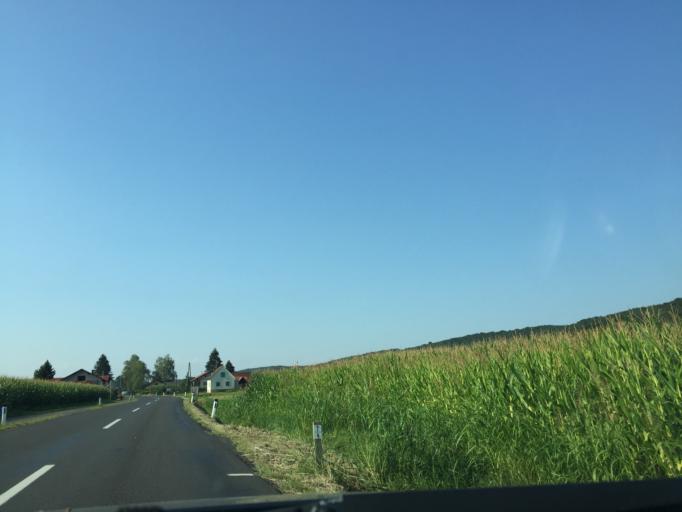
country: AT
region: Styria
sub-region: Politischer Bezirk Suedoststeiermark
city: Deutsch Goritz
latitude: 46.7709
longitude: 15.8607
